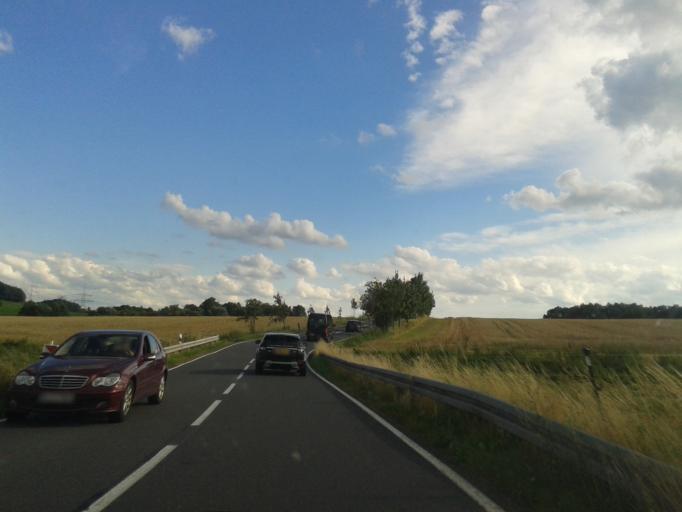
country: DE
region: Saxony
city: Durrrohrsdorf
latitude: 51.0299
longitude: 13.9528
